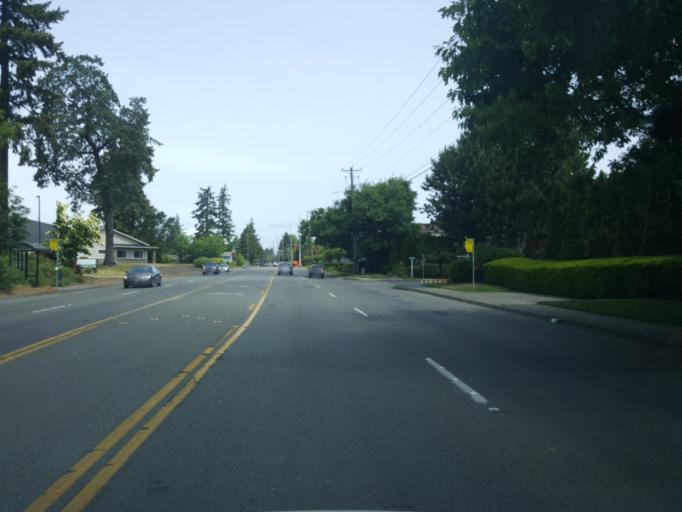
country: US
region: Washington
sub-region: Pierce County
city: Lakewood
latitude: 47.1836
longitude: -122.5085
